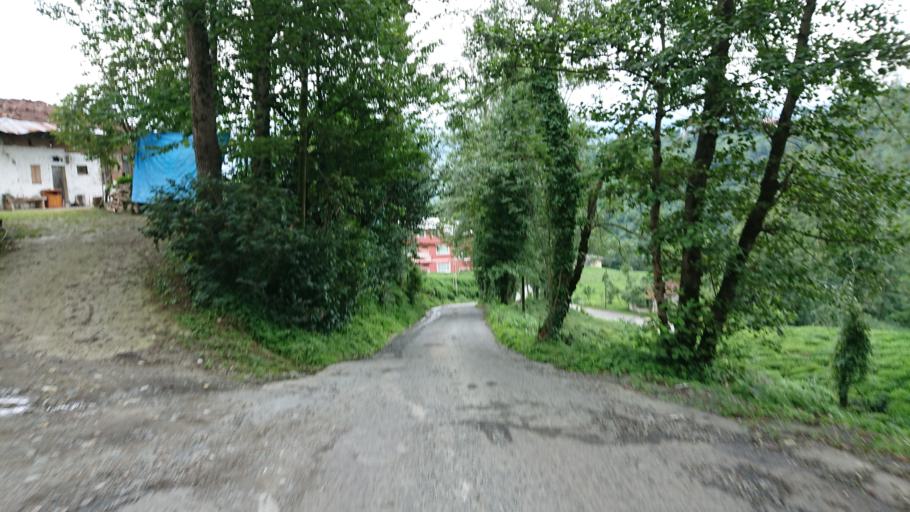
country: TR
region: Rize
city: Rize
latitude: 40.9659
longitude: 40.5132
